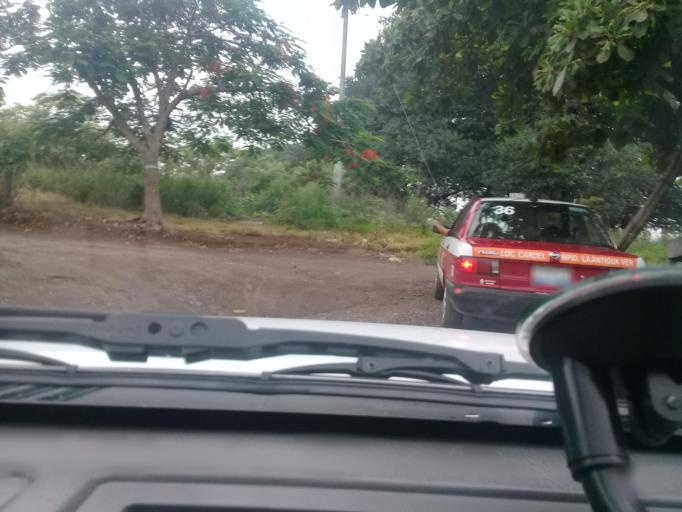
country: MX
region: Veracruz
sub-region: Puente Nacional
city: Chichicaxtle
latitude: 19.3687
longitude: -96.4340
